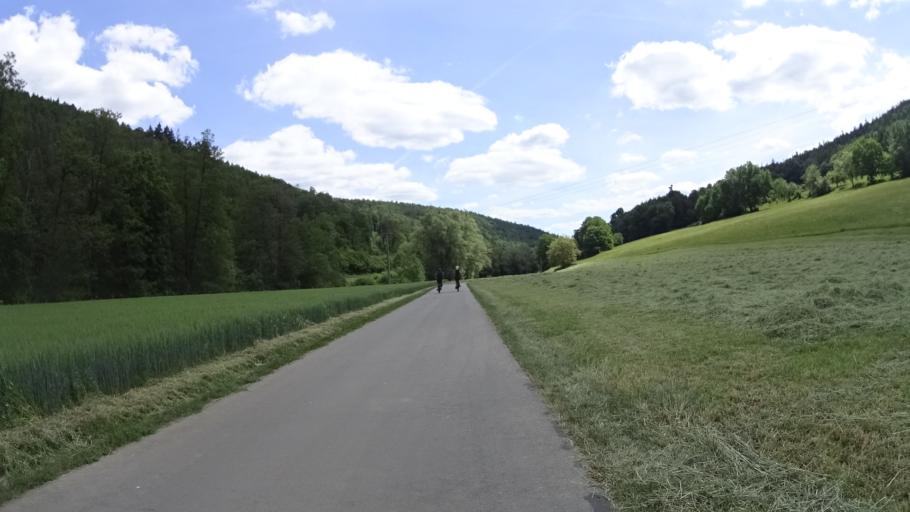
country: DE
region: Bavaria
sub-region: Regierungsbezirk Unterfranken
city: Eichenbuhl
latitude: 49.6902
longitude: 9.3492
